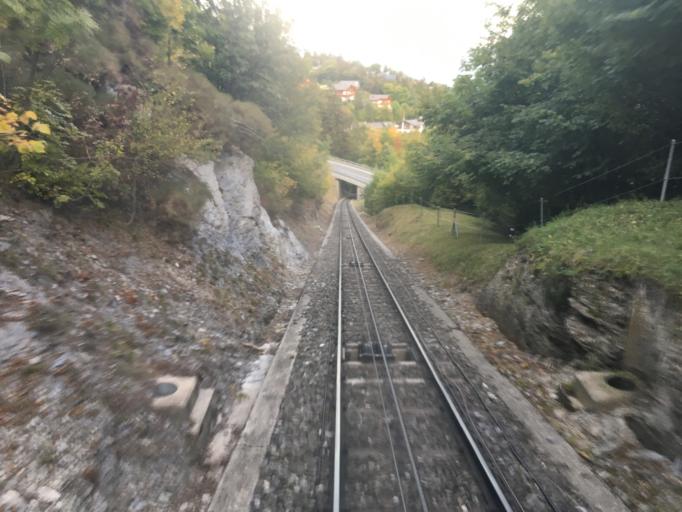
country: CH
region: Valais
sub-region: Sierre District
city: Randogne
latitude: 46.3120
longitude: 7.4944
